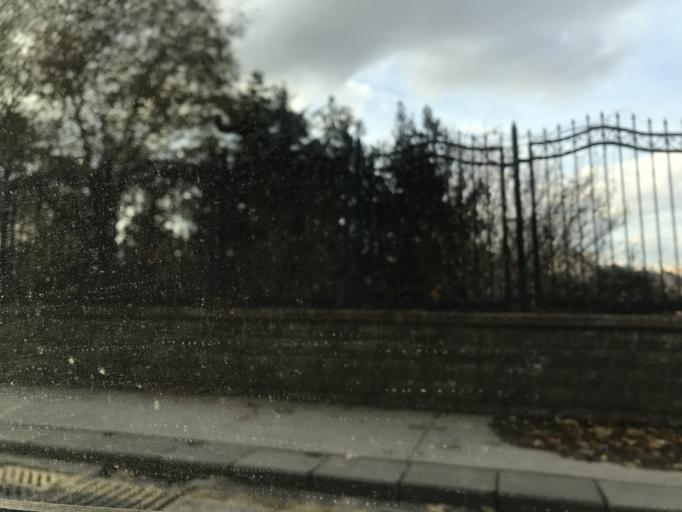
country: TR
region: Ankara
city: Ankara
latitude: 39.9602
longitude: 32.8661
